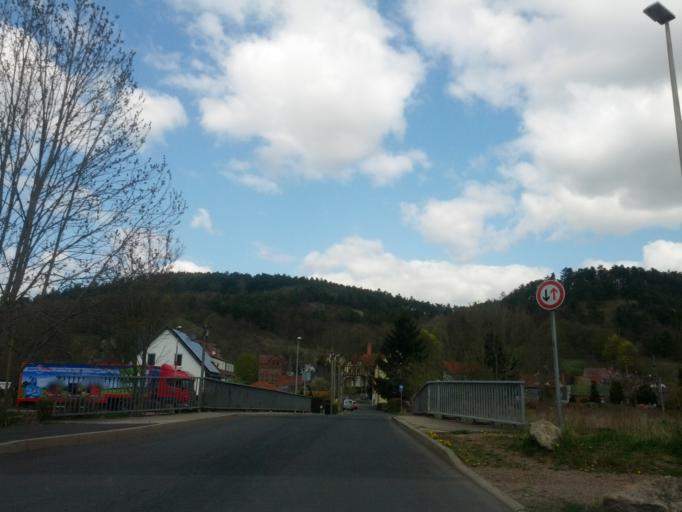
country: DE
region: Thuringia
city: Eisenach
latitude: 50.9656
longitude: 10.3532
